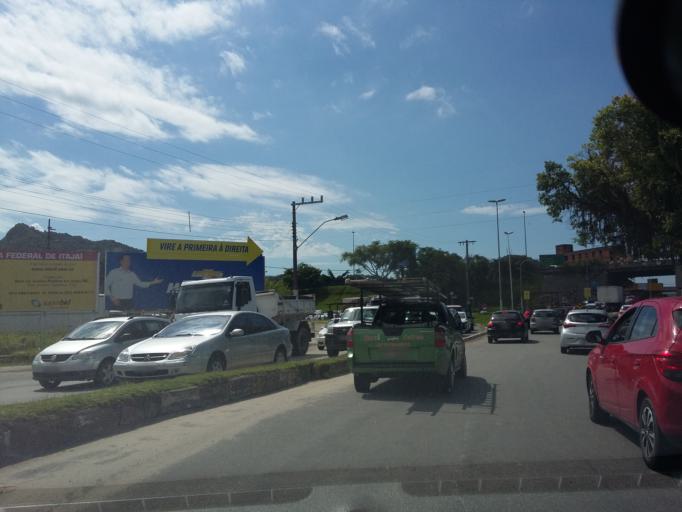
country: BR
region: Santa Catarina
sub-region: Balneario Camboriu
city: Balneario Camboriu
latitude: -27.0005
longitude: -48.6463
